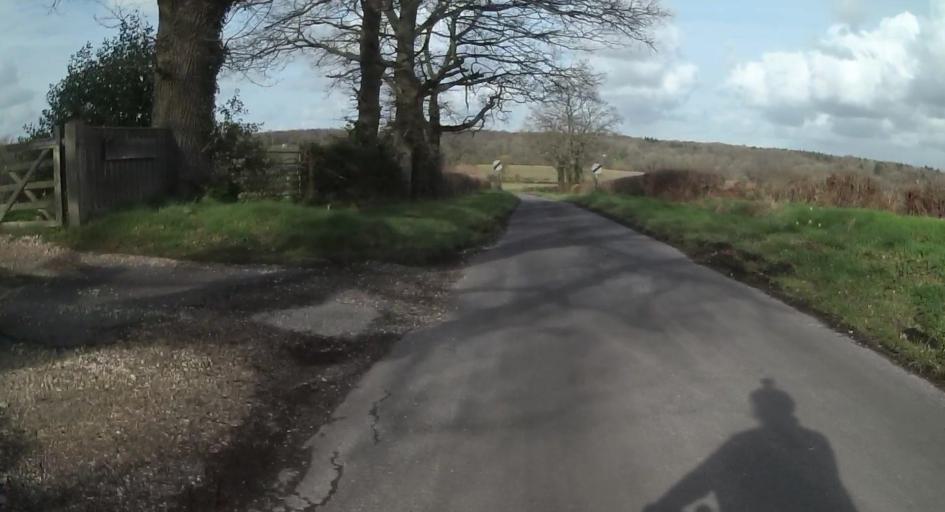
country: GB
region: England
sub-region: West Berkshire
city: Thatcham
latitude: 51.3651
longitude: -1.2543
